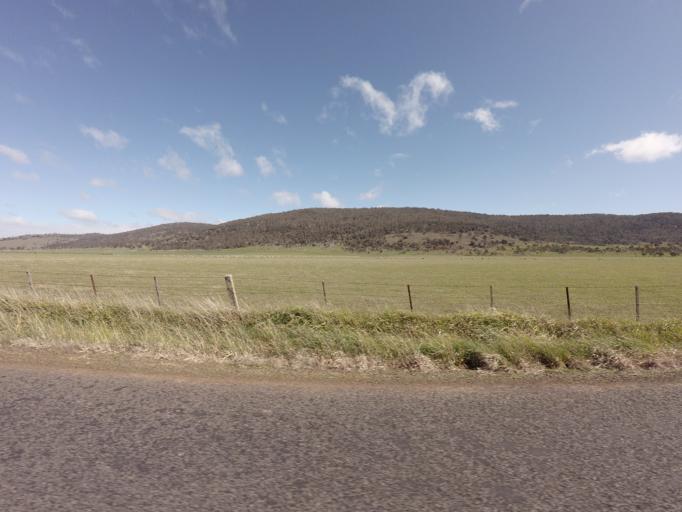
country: AU
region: Tasmania
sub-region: Northern Midlands
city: Evandale
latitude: -41.9717
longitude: 147.4436
